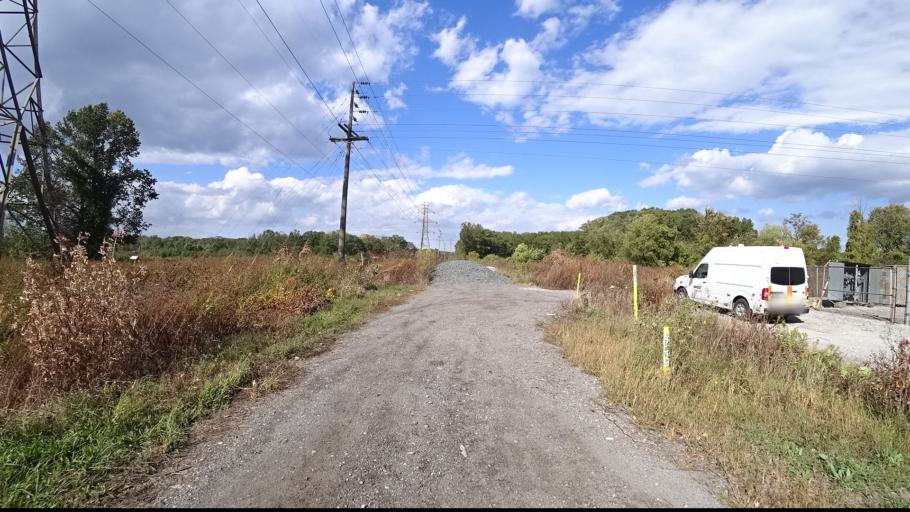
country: US
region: Indiana
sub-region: Porter County
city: Burns Harbor
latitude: 41.6161
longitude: -87.1061
